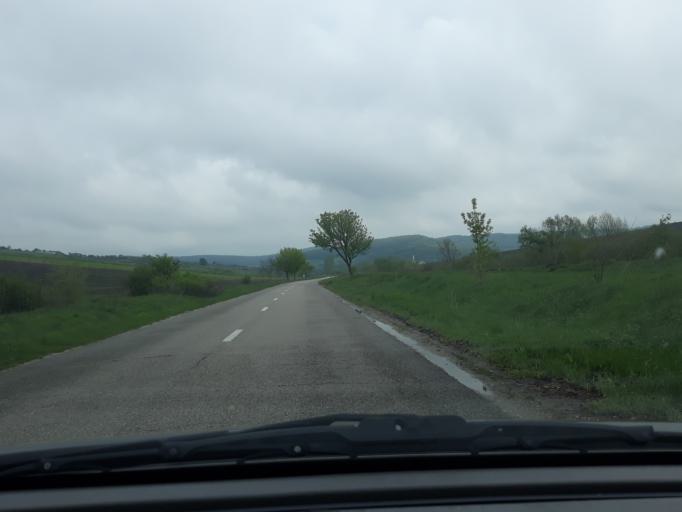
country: RO
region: Salaj
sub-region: Comuna Dobrin
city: Dobrin
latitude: 47.2918
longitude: 23.1106
